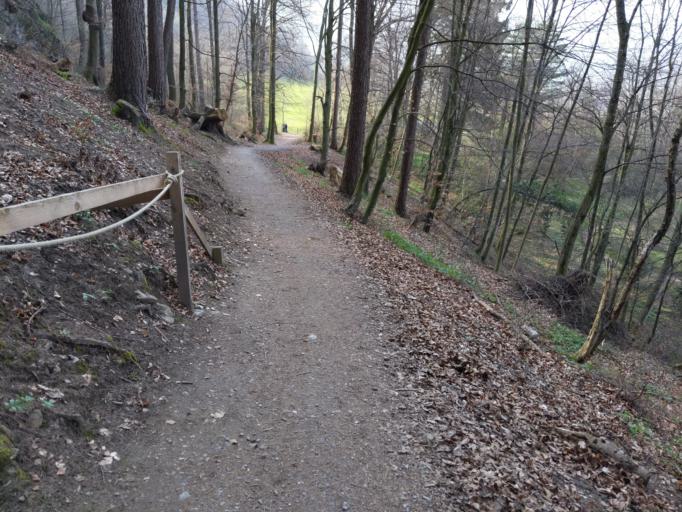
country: CH
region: Saint Gallen
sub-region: Wahlkreis Werdenberg
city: Buchs
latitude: 47.1662
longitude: 9.4583
